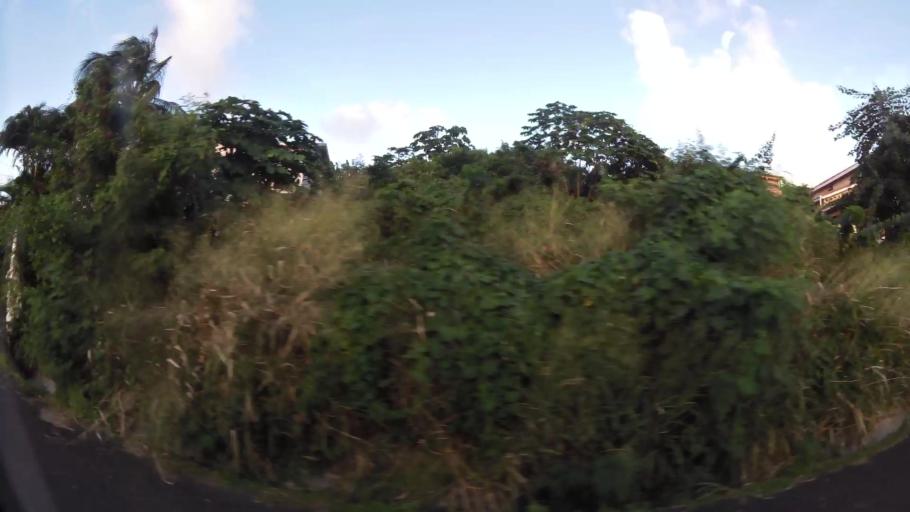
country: LC
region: Gros-Islet
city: Gros Islet
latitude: 14.0662
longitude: -60.9514
